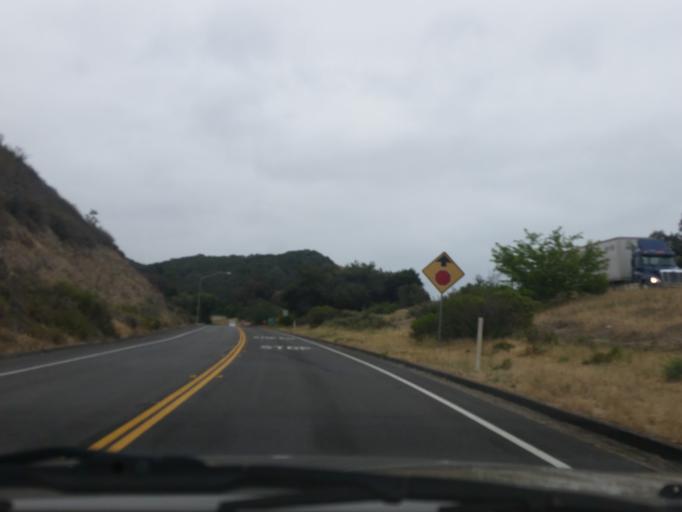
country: US
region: California
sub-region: San Luis Obispo County
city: Avila Beach
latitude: 35.1811
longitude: -120.7002
